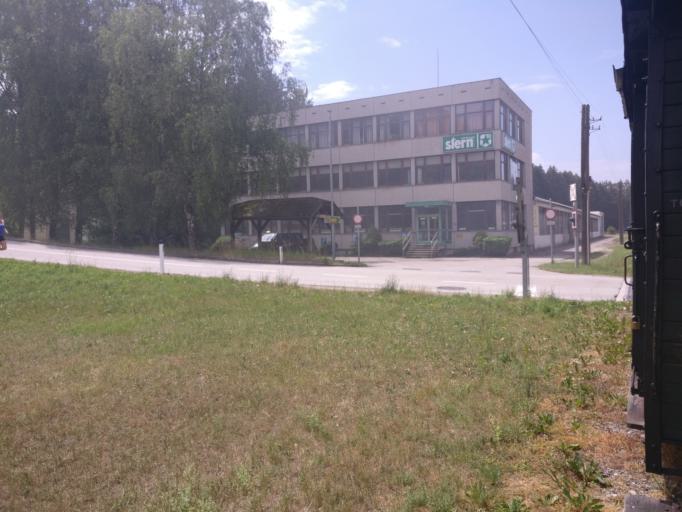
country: AT
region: Upper Austria
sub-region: Politischer Bezirk Steyr-Land
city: Sierning
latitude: 48.0200
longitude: 14.3259
